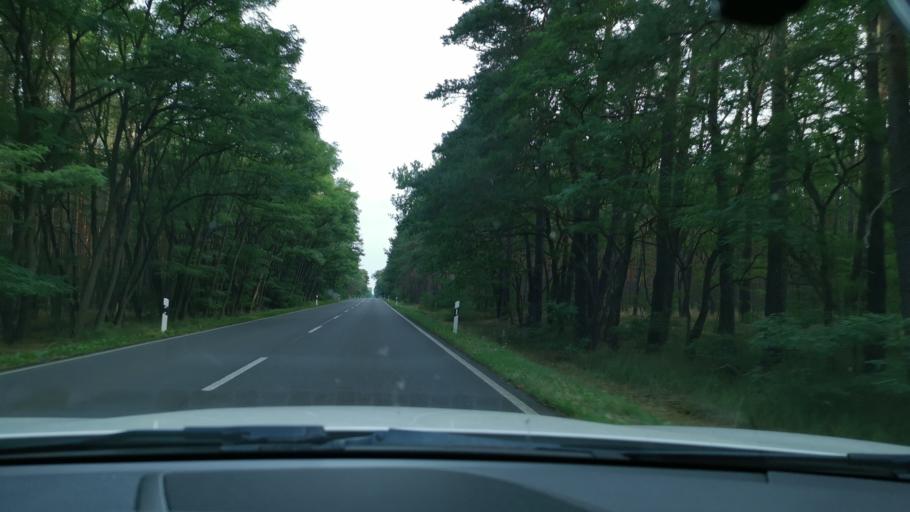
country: DE
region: Saxony-Anhalt
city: Holzdorf
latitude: 51.8634
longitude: 13.1460
